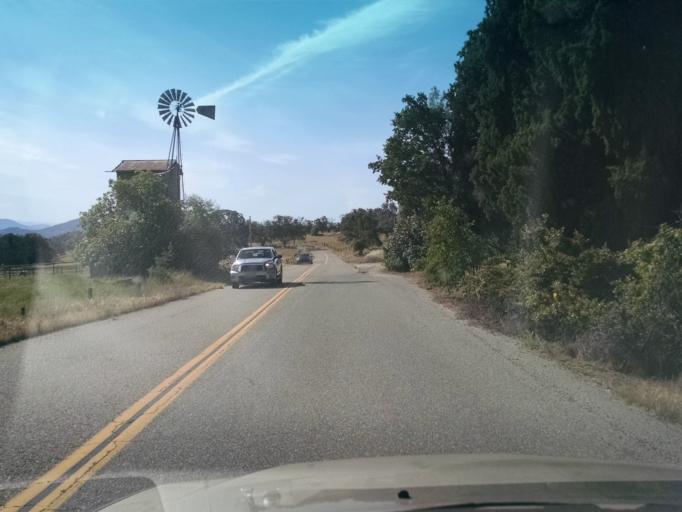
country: US
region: California
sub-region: Madera County
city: Yosemite Lakes
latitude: 37.1198
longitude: -119.7011
